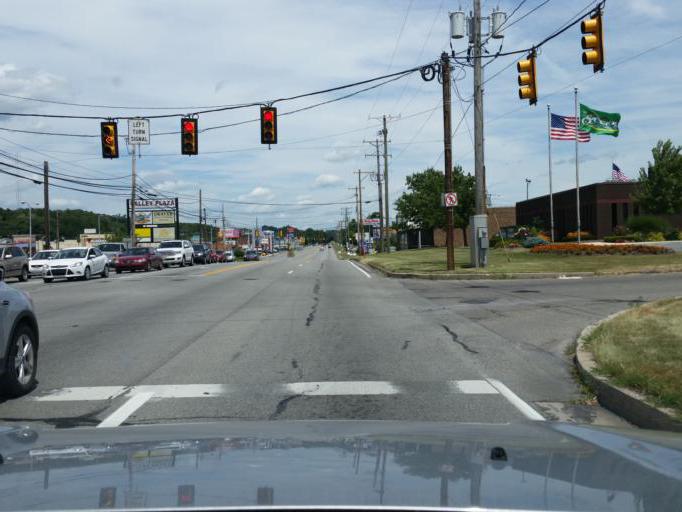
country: US
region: Pennsylvania
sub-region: Blair County
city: Lakemont
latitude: 40.4844
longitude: -78.4006
